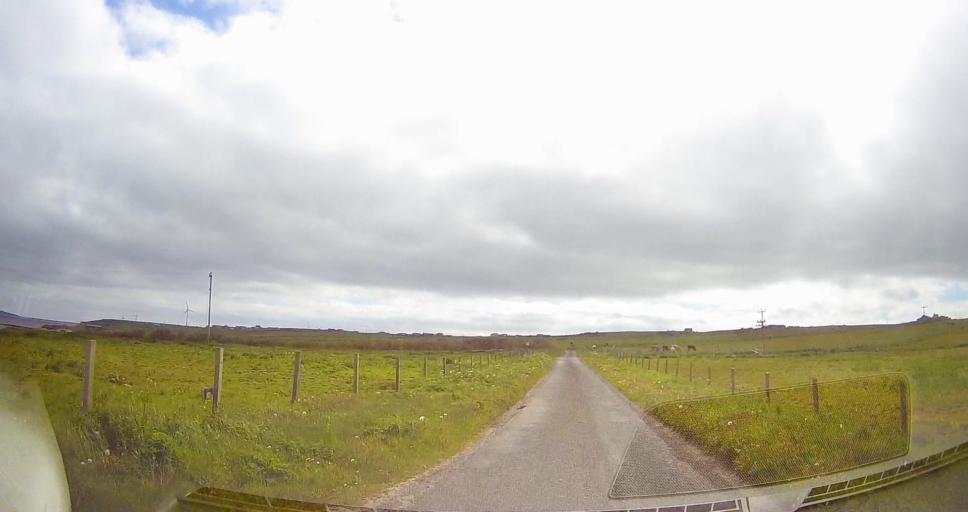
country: GB
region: Scotland
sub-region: Orkney Islands
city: Kirkwall
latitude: 58.9491
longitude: -2.7188
